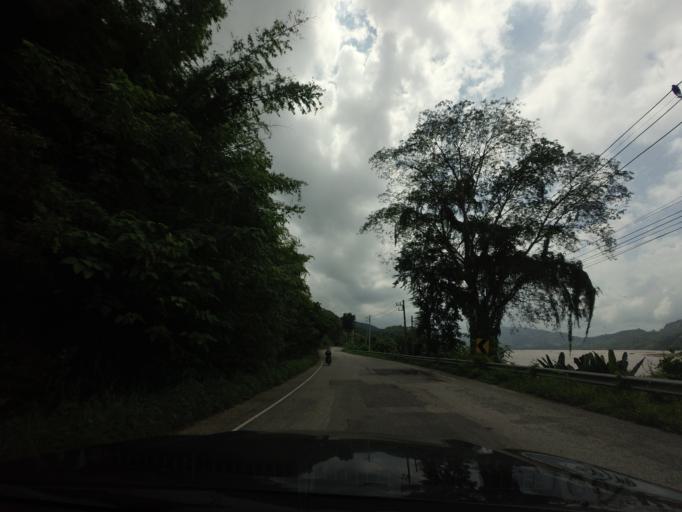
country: TH
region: Loei
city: Pak Chom
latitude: 18.0525
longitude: 101.7756
